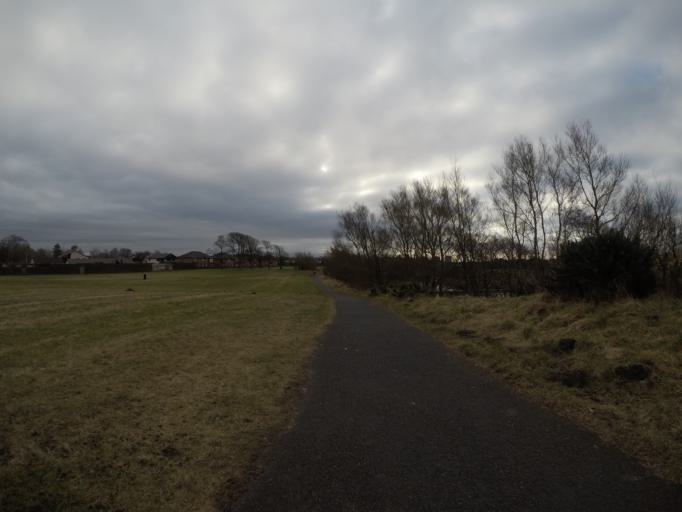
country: GB
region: Scotland
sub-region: North Ayrshire
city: Irvine
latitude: 55.6222
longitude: -4.6760
